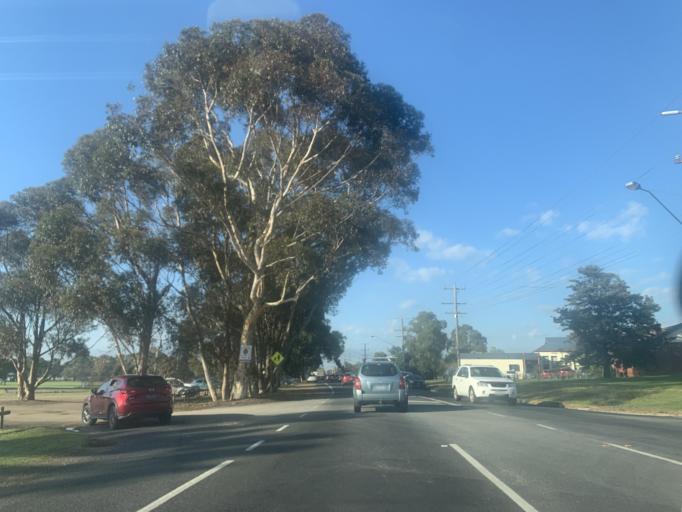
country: AU
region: Victoria
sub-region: Mornington Peninsula
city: Hastings
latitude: -38.3029
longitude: 145.1918
